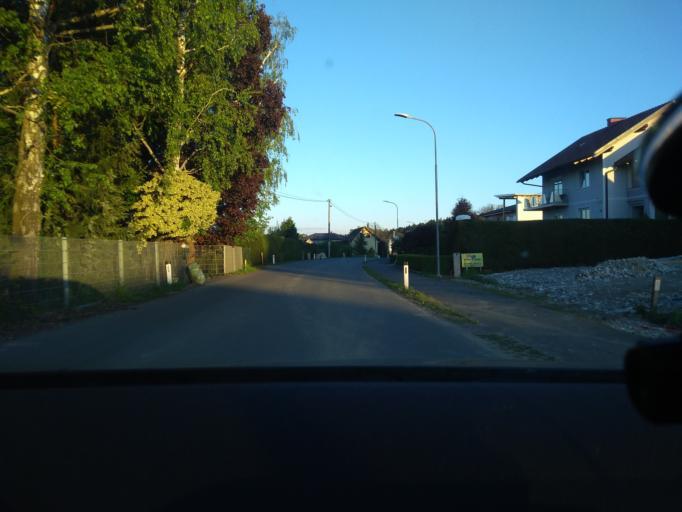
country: AT
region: Styria
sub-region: Politischer Bezirk Graz-Umgebung
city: Lieboch
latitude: 46.9639
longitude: 15.3118
